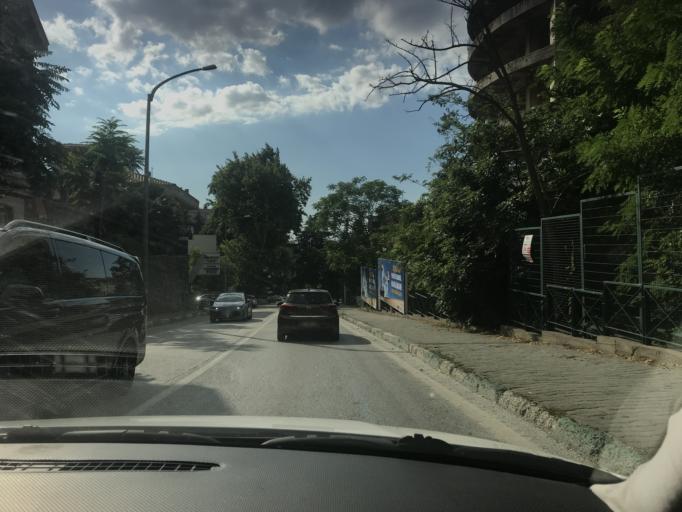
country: TR
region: Bursa
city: Yildirim
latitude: 40.2034
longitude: 29.0223
